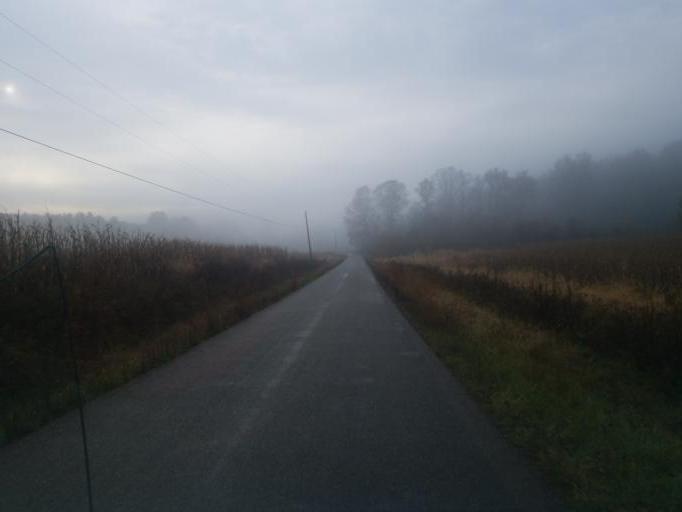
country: US
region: Ohio
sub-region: Athens County
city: Glouster
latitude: 39.4665
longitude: -81.9375
